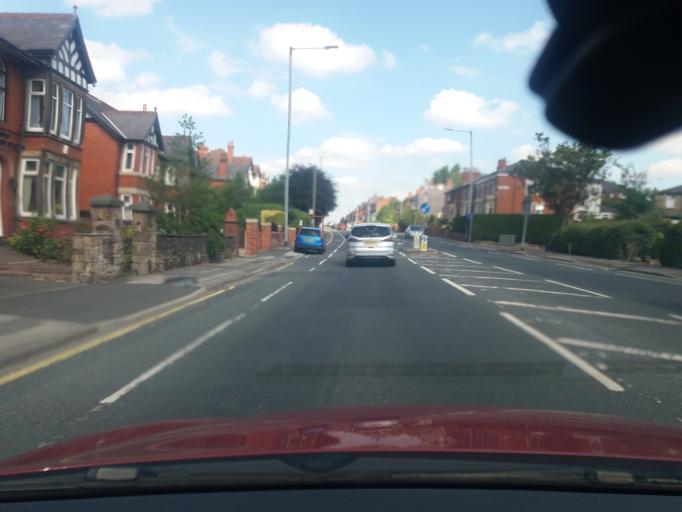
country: GB
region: England
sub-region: Lancashire
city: Chorley
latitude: 53.6436
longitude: -2.6212
